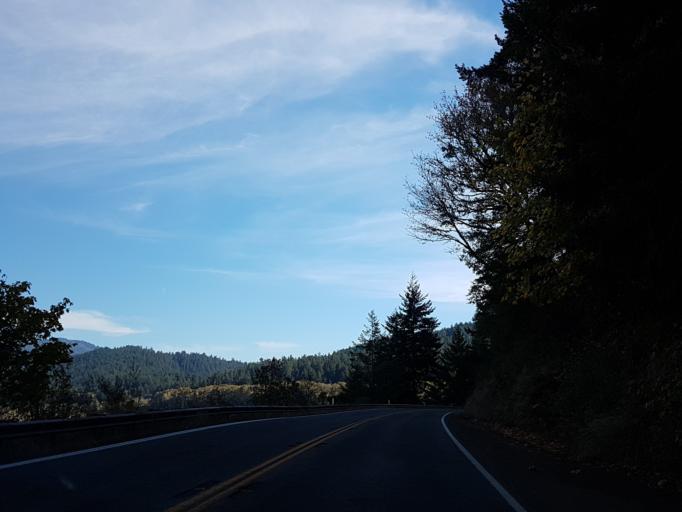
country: US
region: California
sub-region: Humboldt County
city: Rio Dell
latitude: 40.4262
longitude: -123.9810
